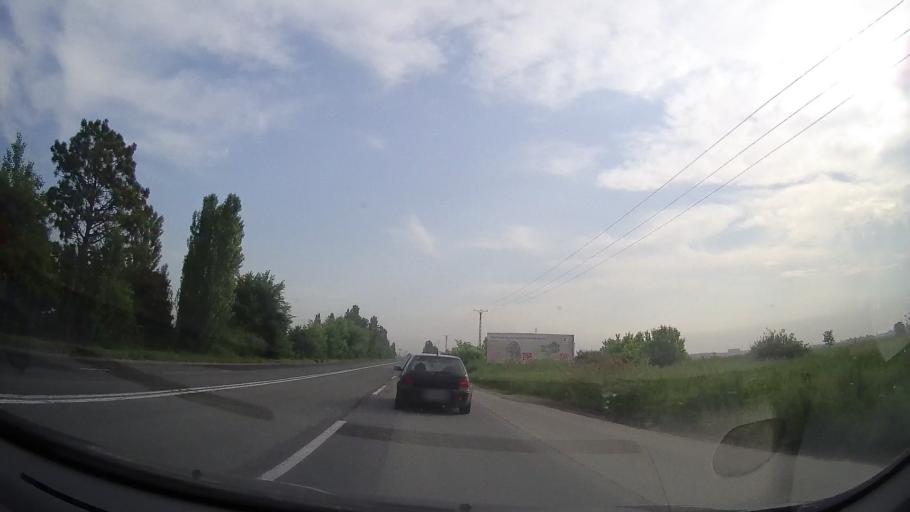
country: RO
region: Timis
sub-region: Comuna Sag
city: Sag
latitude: 45.6895
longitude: 21.1731
